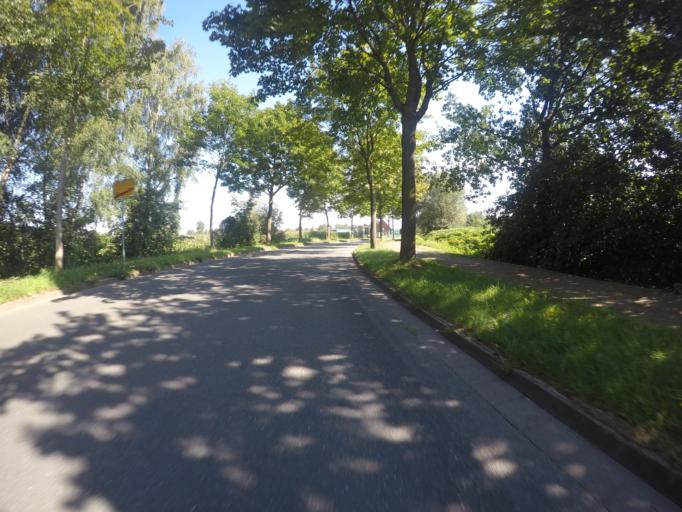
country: DE
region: North Rhine-Westphalia
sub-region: Regierungsbezirk Munster
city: Isselburg
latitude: 51.8154
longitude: 6.5401
